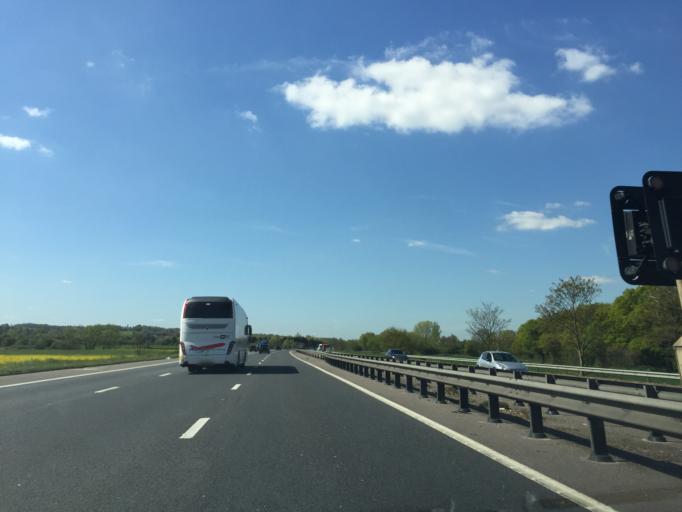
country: GB
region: England
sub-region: Essex
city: Theydon Bois
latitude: 51.6517
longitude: 0.1008
